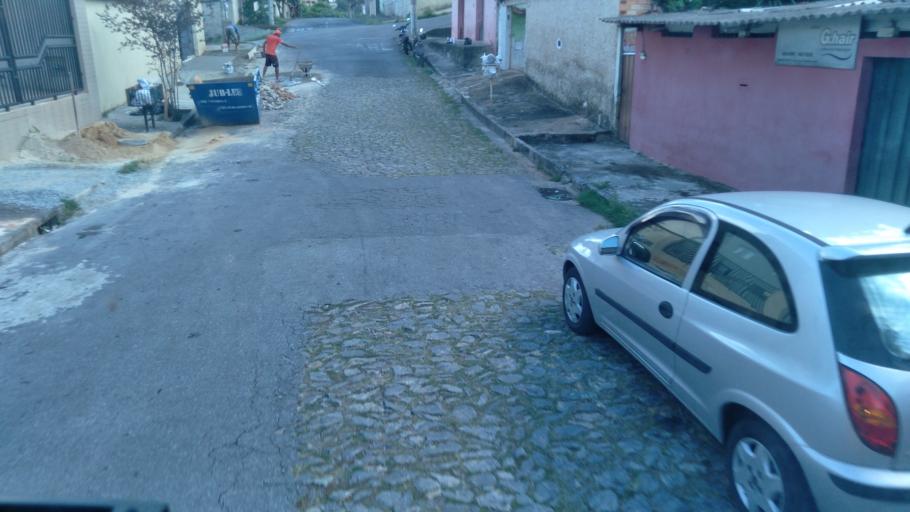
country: BR
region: Minas Gerais
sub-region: Belo Horizonte
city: Belo Horizonte
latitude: -19.8523
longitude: -43.9104
